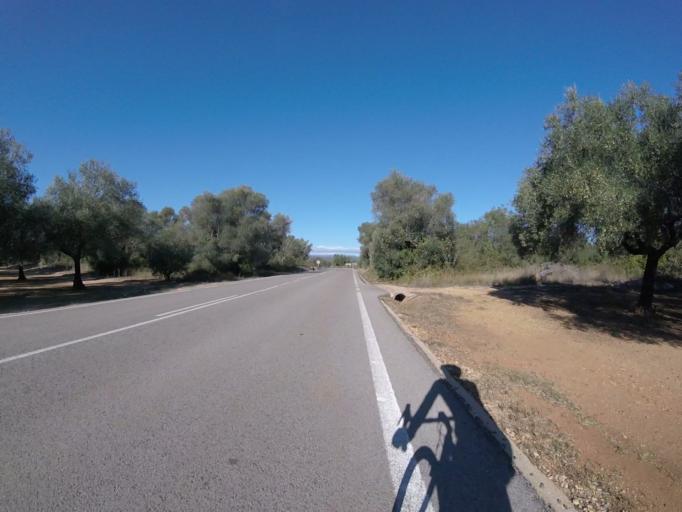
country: ES
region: Valencia
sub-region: Provincia de Castello
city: Cervera del Maestre
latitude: 40.4766
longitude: 0.2220
